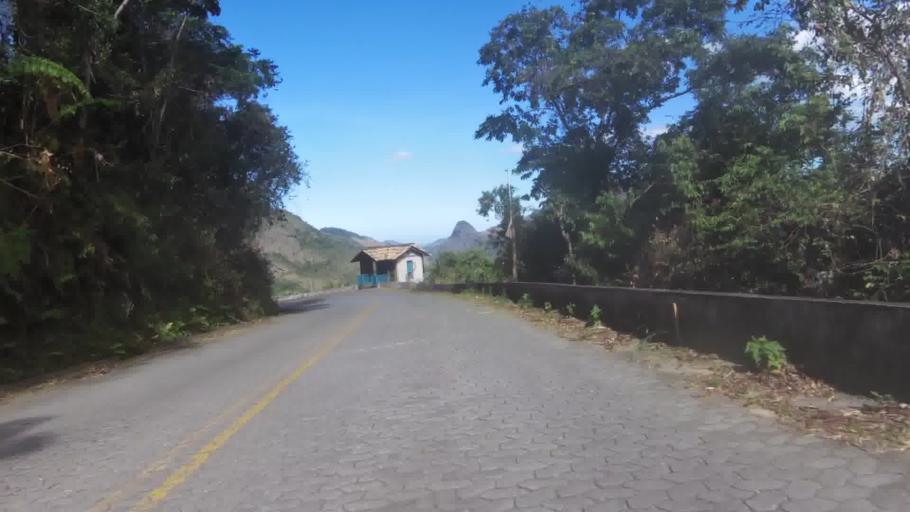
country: BR
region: Espirito Santo
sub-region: Vargem Alta
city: Vargem Alta
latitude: -20.6924
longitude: -40.9350
